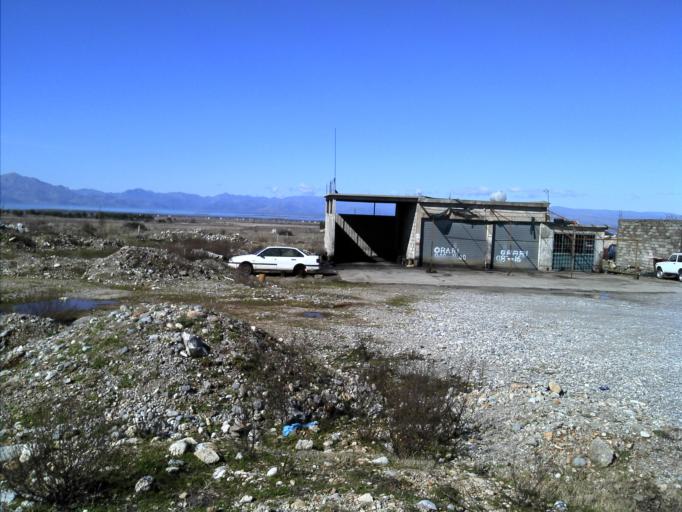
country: AL
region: Shkoder
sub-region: Rrethi i Malesia e Madhe
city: Koplik
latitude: 42.2401
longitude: 19.4239
